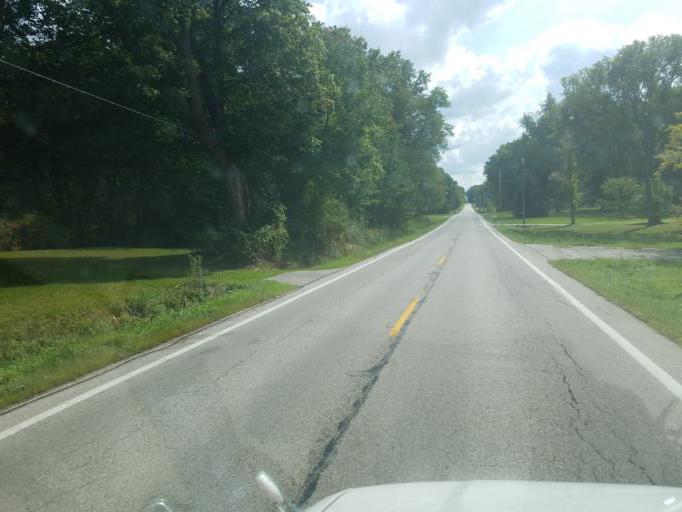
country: US
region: Ohio
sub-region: Portage County
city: Hiram
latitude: 41.3708
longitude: -81.1431
